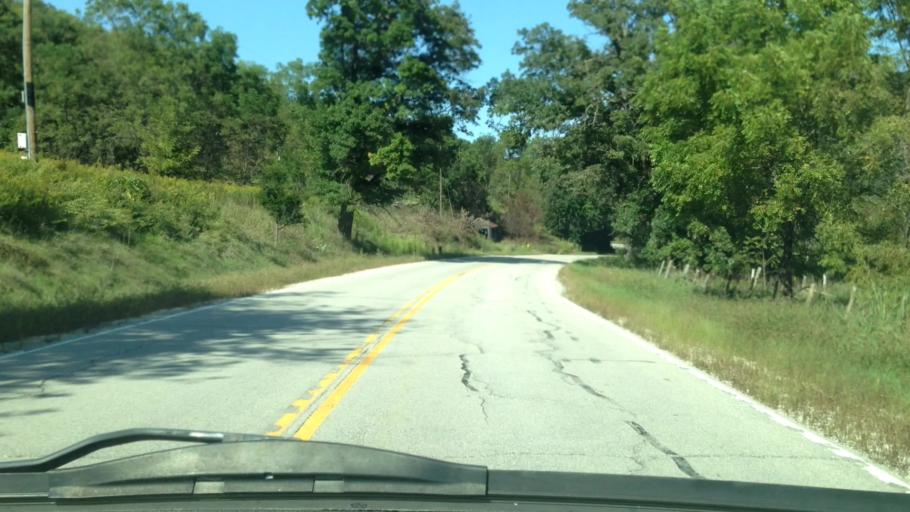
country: US
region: Minnesota
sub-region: Fillmore County
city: Rushford
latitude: 43.6687
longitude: -91.7940
